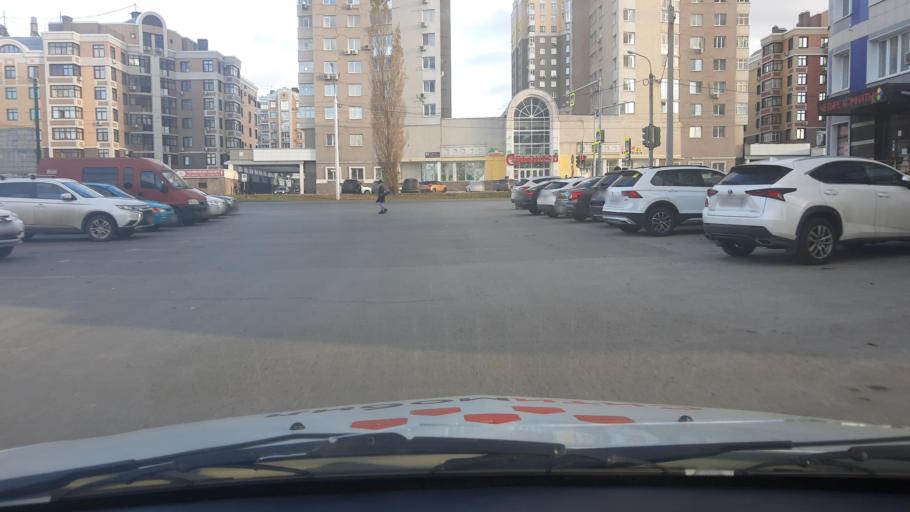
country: RU
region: Bashkortostan
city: Ufa
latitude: 54.7695
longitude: 56.0113
